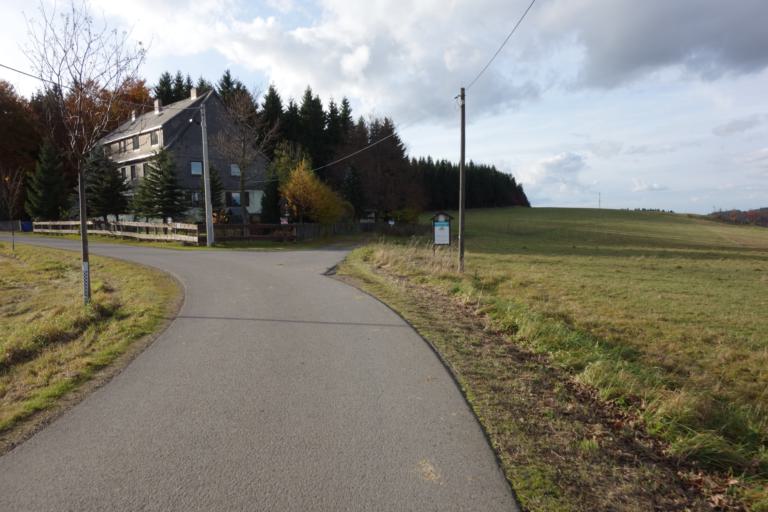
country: DE
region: Saxony
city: Rechenberg-Bienenmuhle
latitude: 50.7225
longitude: 13.5863
